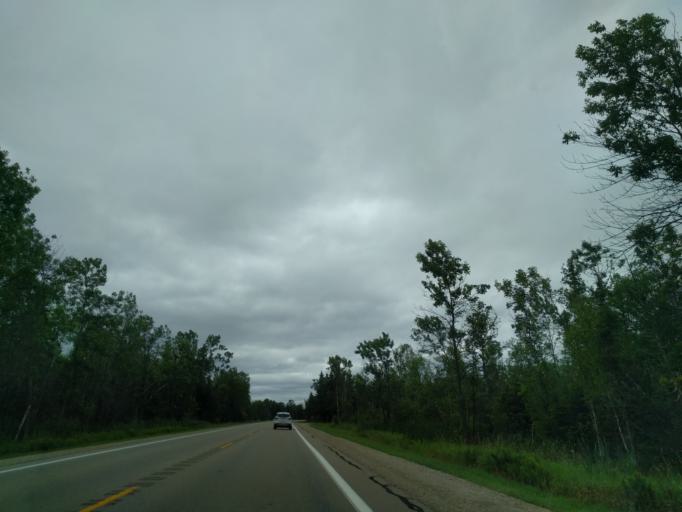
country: US
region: Michigan
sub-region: Delta County
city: Escanaba
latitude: 45.5120
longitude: -87.2879
